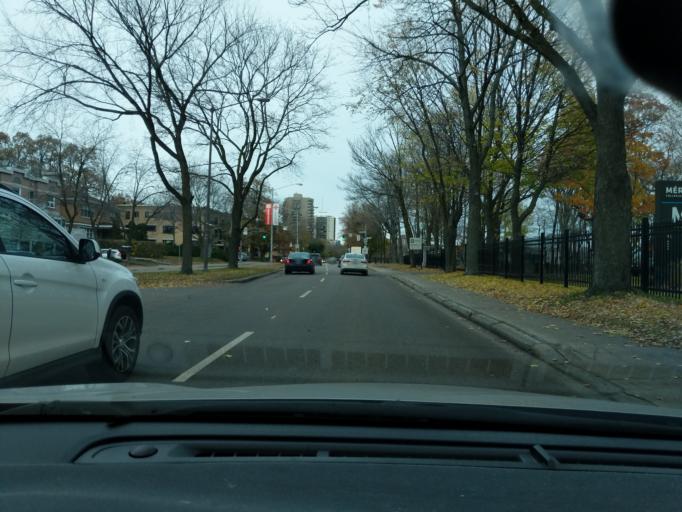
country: CA
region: Quebec
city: Quebec
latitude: 46.7964
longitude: -71.2335
